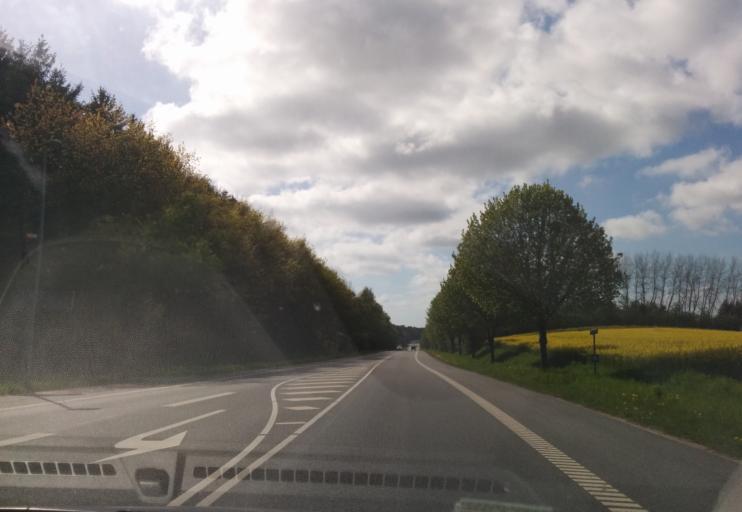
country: DK
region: South Denmark
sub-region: Assens Kommune
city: Vissenbjerg
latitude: 55.3905
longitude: 10.1293
